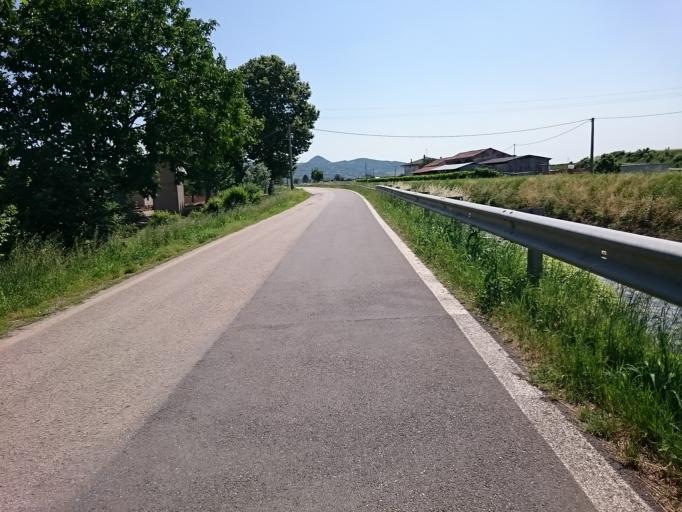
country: IT
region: Veneto
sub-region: Provincia di Padova
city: Lozzo Atestino
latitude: 45.2593
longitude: 11.5973
